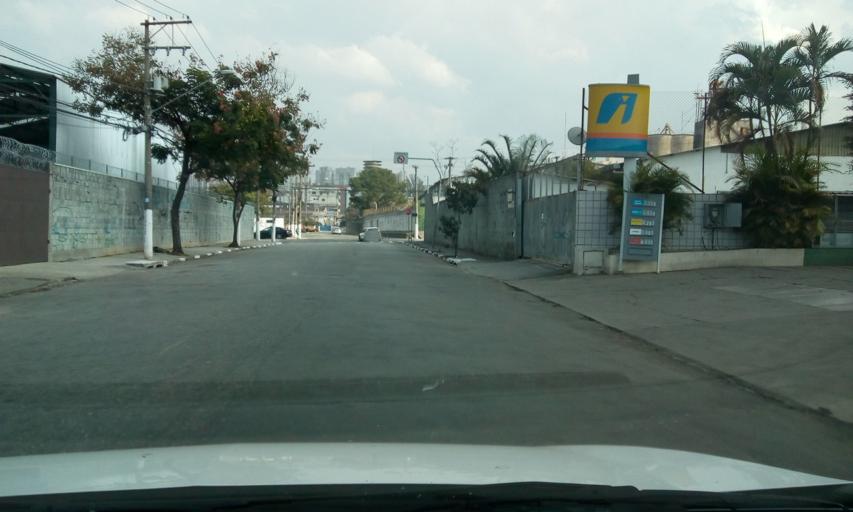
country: BR
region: Sao Paulo
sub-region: Osasco
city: Osasco
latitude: -23.5456
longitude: -46.7386
